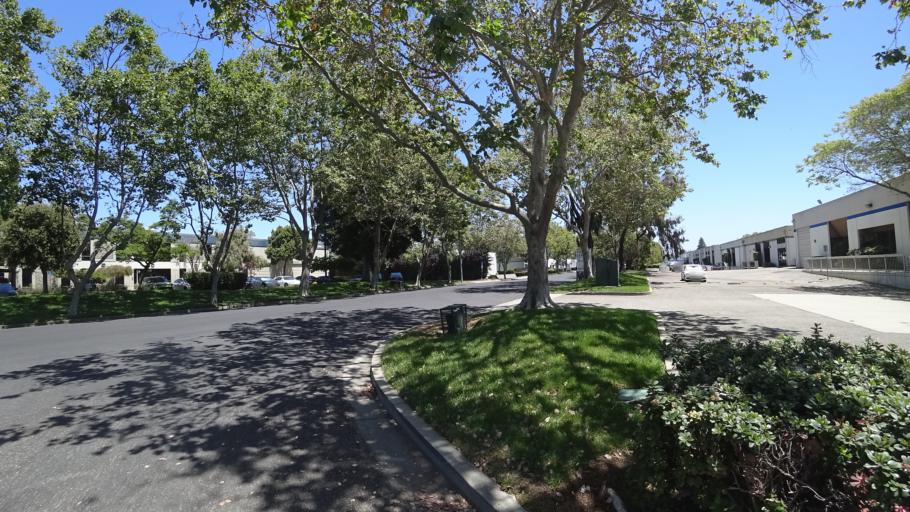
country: US
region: California
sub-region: Alameda County
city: San Lorenzo
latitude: 37.6357
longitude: -122.1264
